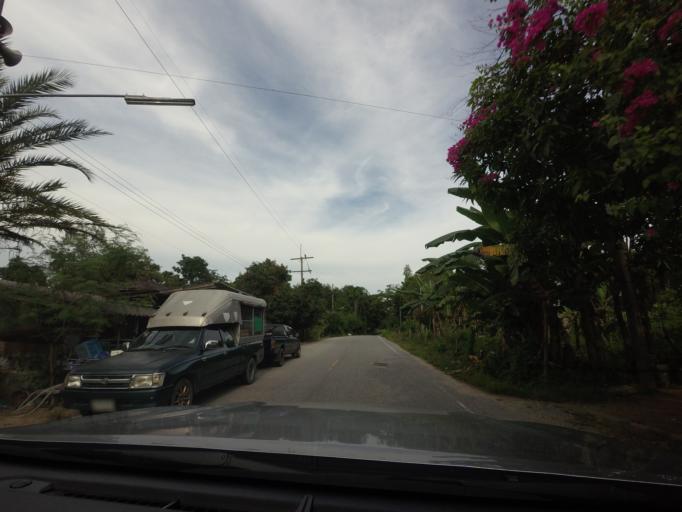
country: TH
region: Narathiwat
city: Rueso
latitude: 6.3530
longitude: 101.4713
